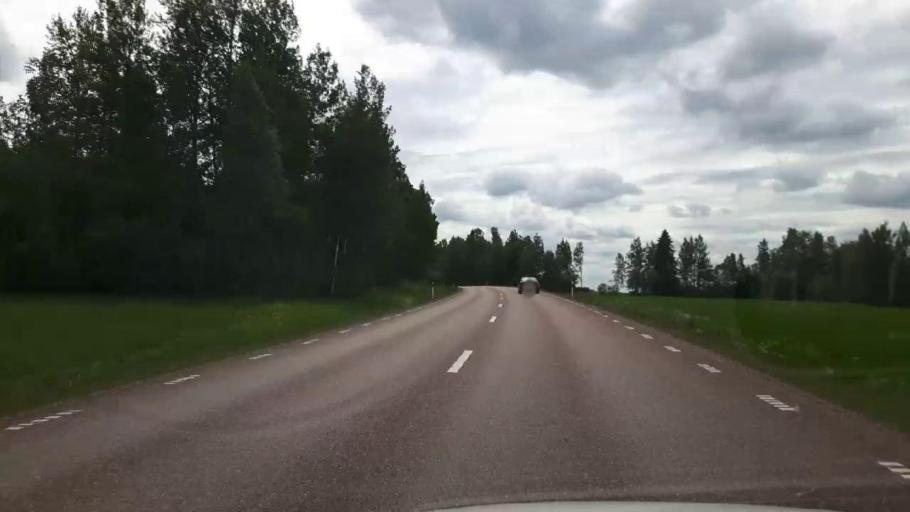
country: SE
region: Dalarna
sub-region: Hedemora Kommun
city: Hedemora
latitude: 60.3380
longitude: 15.9447
